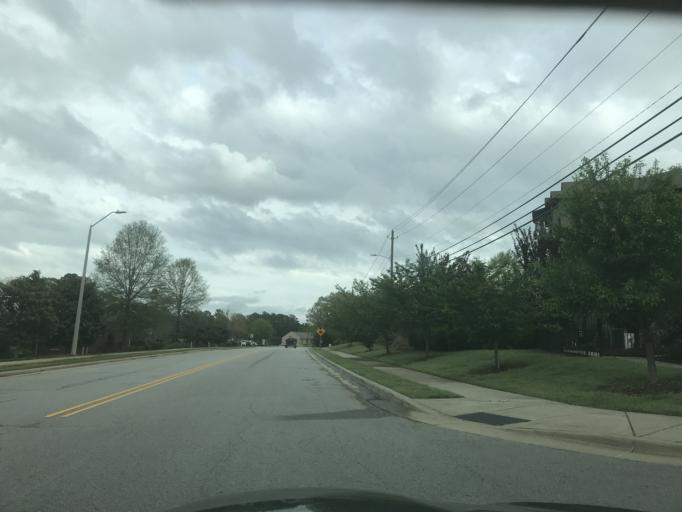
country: US
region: North Carolina
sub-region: Wake County
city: West Raleigh
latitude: 35.7477
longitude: -78.6772
